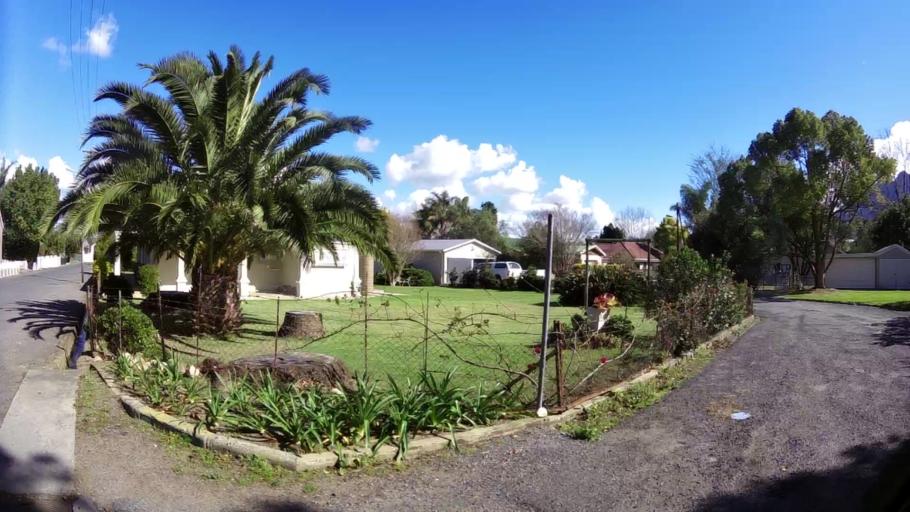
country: ZA
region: Western Cape
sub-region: Overberg District Municipality
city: Swellendam
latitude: -34.0192
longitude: 20.4500
